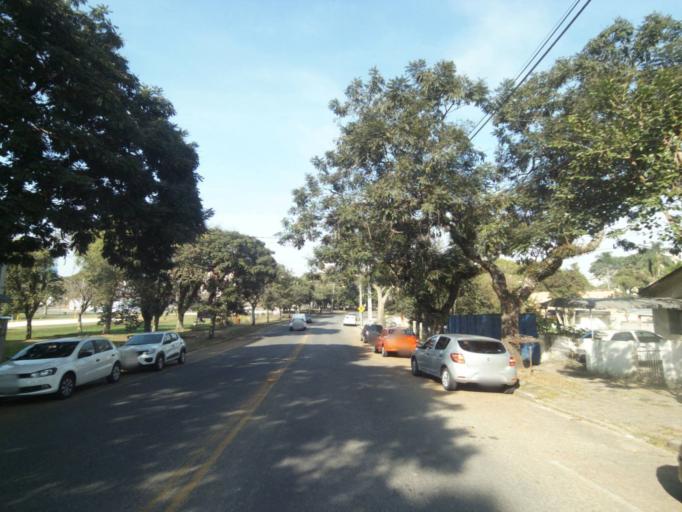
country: BR
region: Parana
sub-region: Curitiba
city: Curitiba
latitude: -25.4608
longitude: -49.2801
